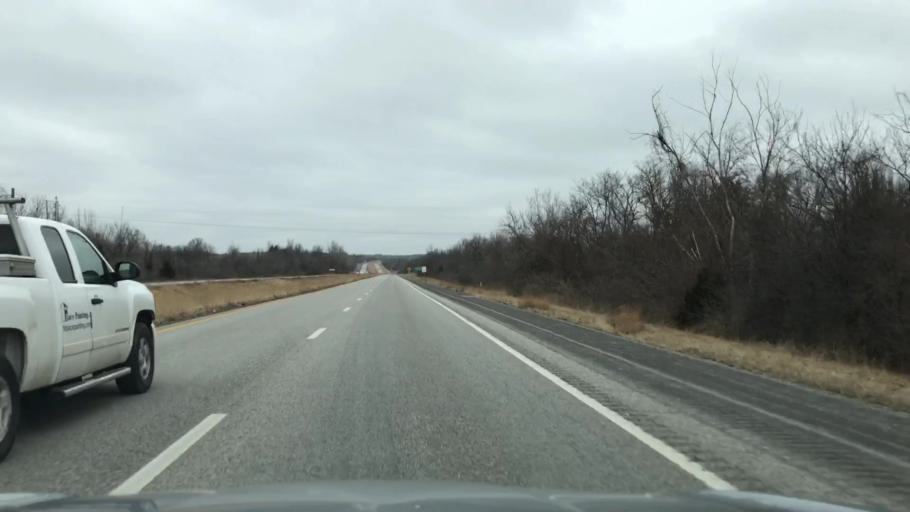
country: US
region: Missouri
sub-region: Clay County
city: Liberty
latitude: 39.2066
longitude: -94.4046
